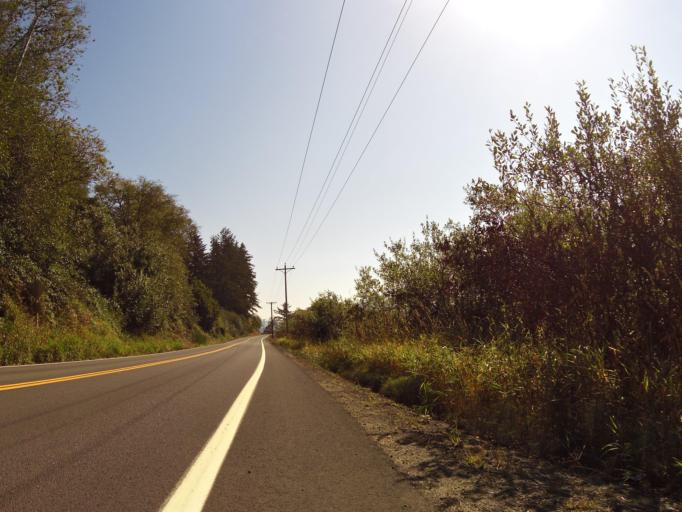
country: US
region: Oregon
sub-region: Tillamook County
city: Pacific City
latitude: 45.1841
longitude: -123.9458
